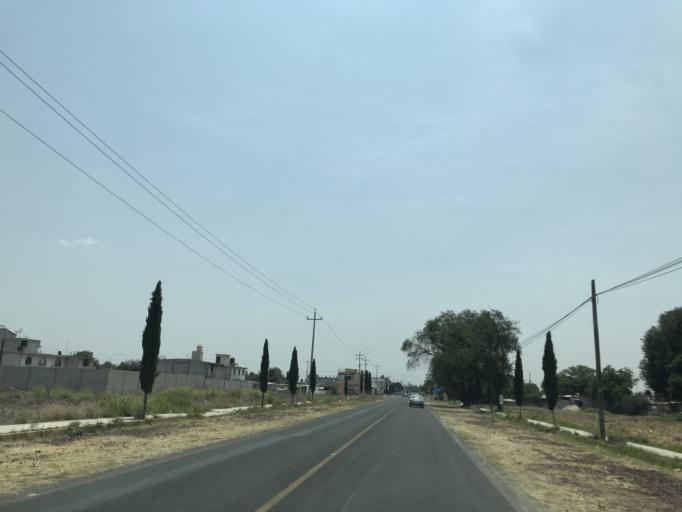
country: MX
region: Tlaxcala
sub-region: Ixtacuixtla de Mariano Matamoros
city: Villa Mariano Matamoros
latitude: 19.3095
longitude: -98.3804
